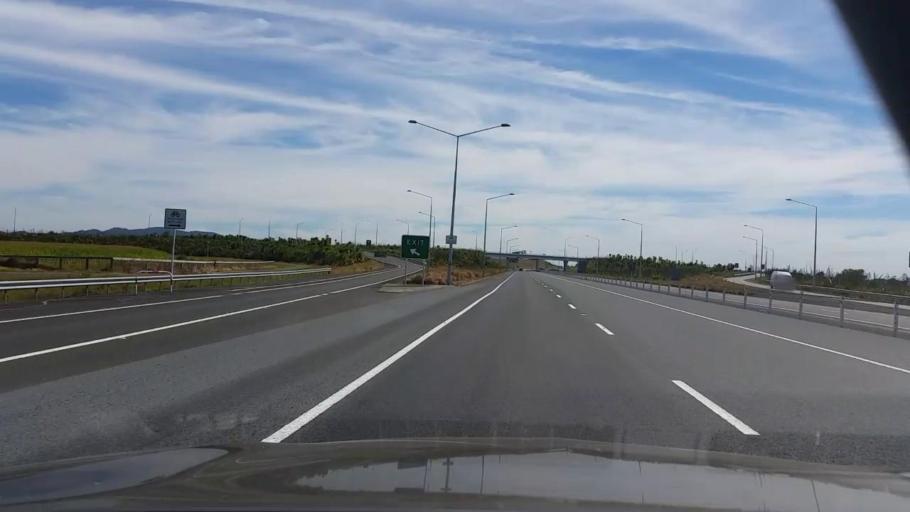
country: NZ
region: Waikato
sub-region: Hamilton City
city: Hamilton
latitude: -37.7361
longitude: 175.2111
